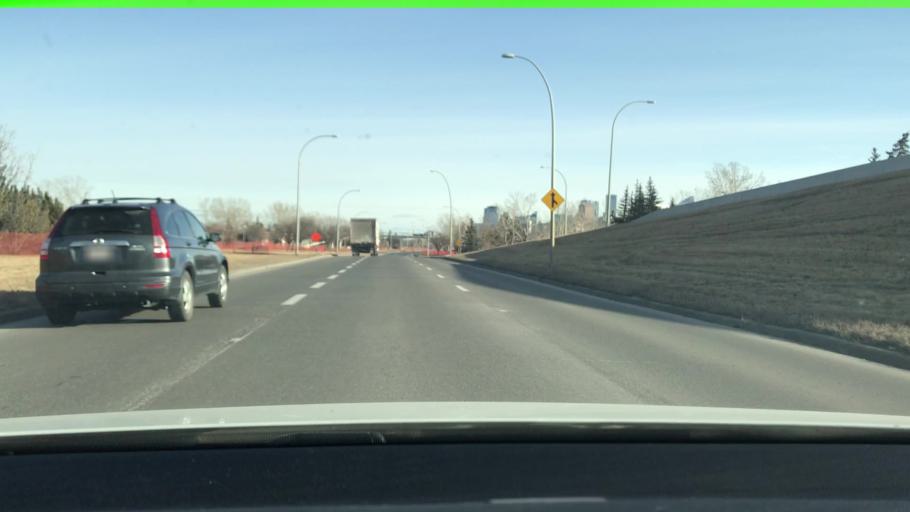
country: CA
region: Alberta
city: Calgary
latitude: 51.0484
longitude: -114.1150
